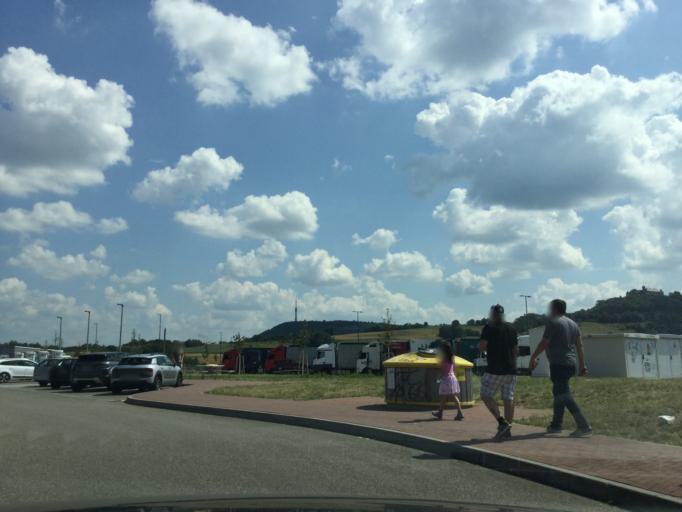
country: DE
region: Baden-Wuerttemberg
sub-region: Regierungsbezirk Stuttgart
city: Waldenburg
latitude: 49.2056
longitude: 9.6393
